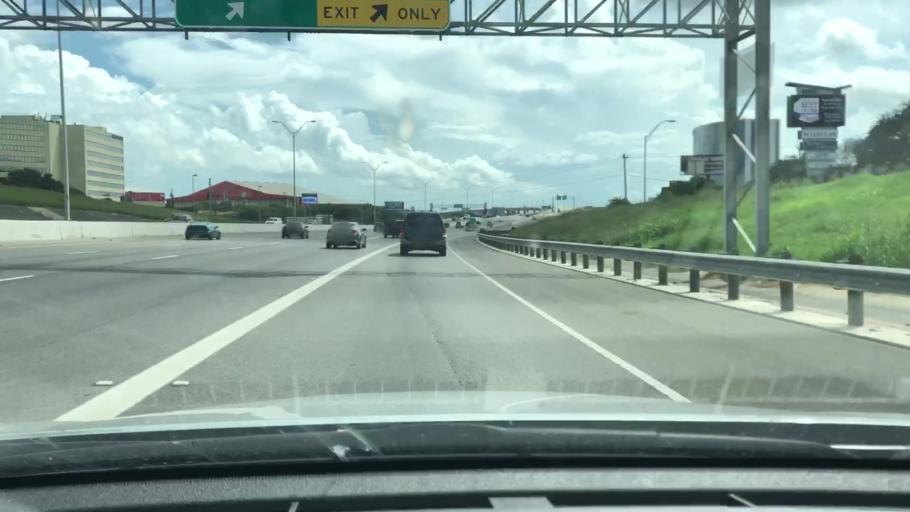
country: US
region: Texas
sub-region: Bexar County
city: Castle Hills
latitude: 29.5317
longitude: -98.4861
